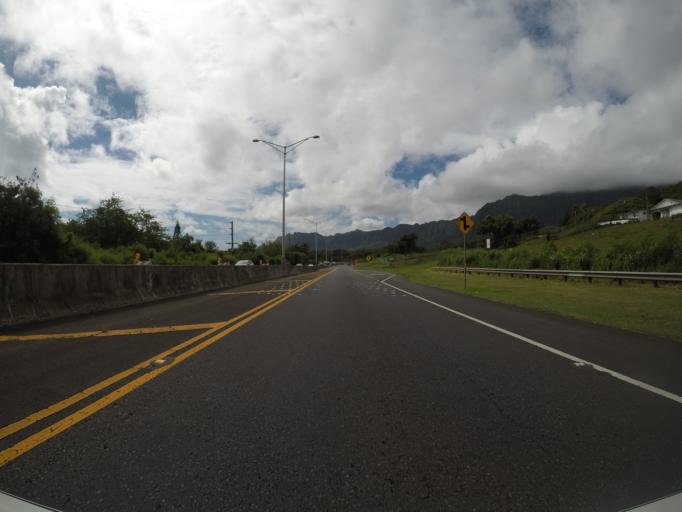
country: US
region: Hawaii
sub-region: Honolulu County
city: Waimanalo
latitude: 21.3561
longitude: -157.7312
